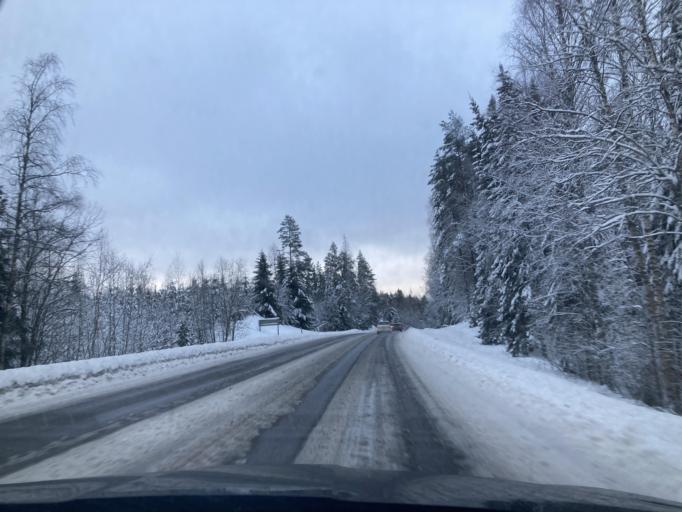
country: FI
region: Central Finland
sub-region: Jaemsae
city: Kuhmoinen
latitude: 61.4439
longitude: 25.1724
